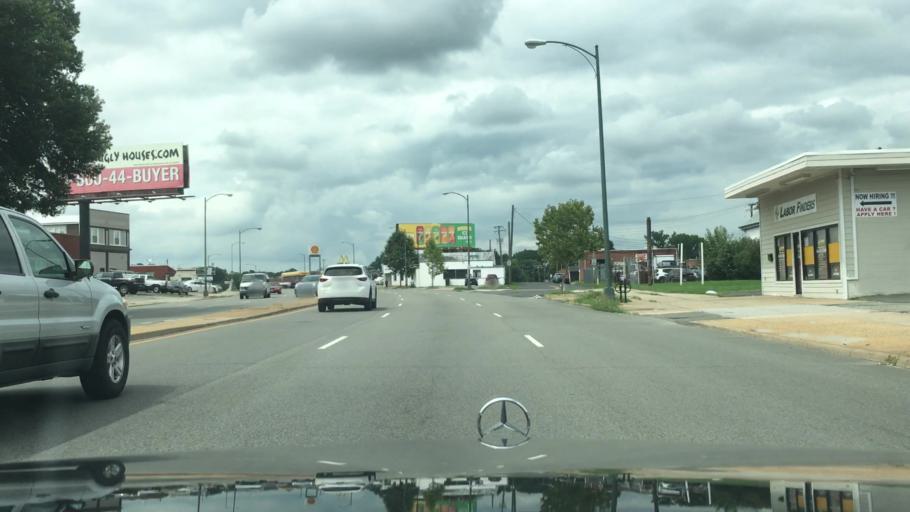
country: US
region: Virginia
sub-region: City of Richmond
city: Richmond
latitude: 37.5603
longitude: -77.4424
